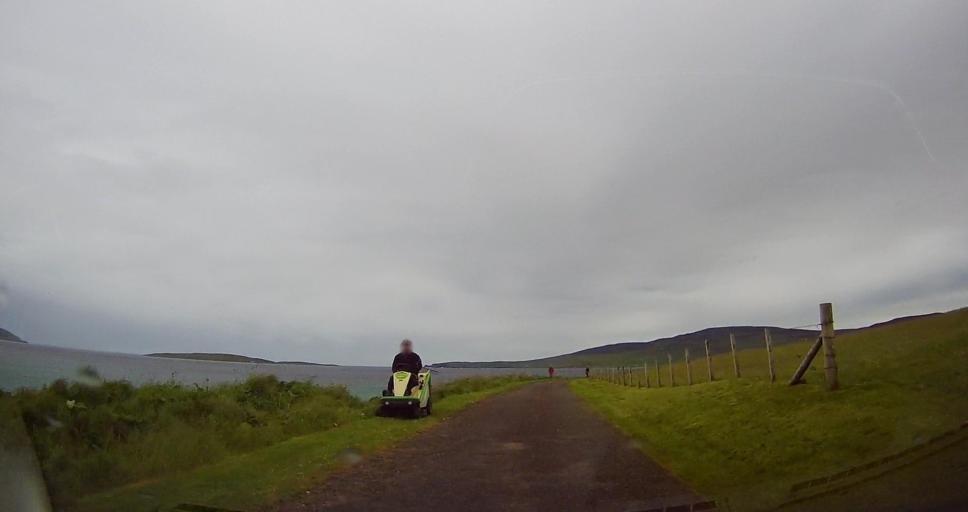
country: GB
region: Scotland
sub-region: Orkney Islands
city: Orkney
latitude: 59.1215
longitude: -3.0851
